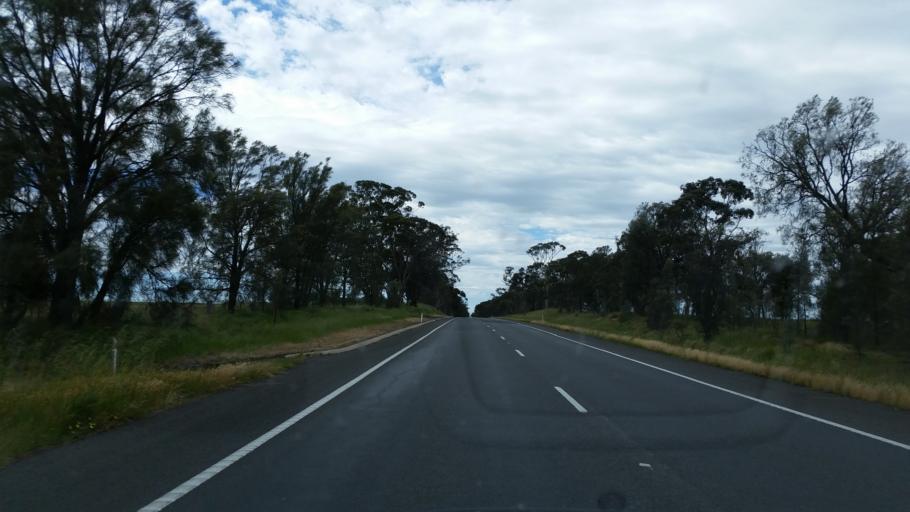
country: AU
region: South Australia
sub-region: Tatiara
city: Bordertown
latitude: -36.3484
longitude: 140.9992
